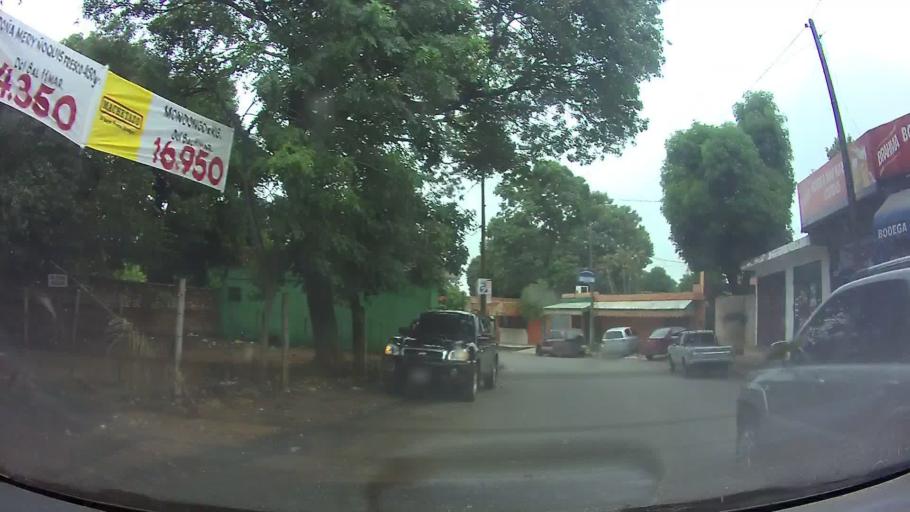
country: PY
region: Central
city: San Lorenzo
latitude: -25.3393
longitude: -57.4980
